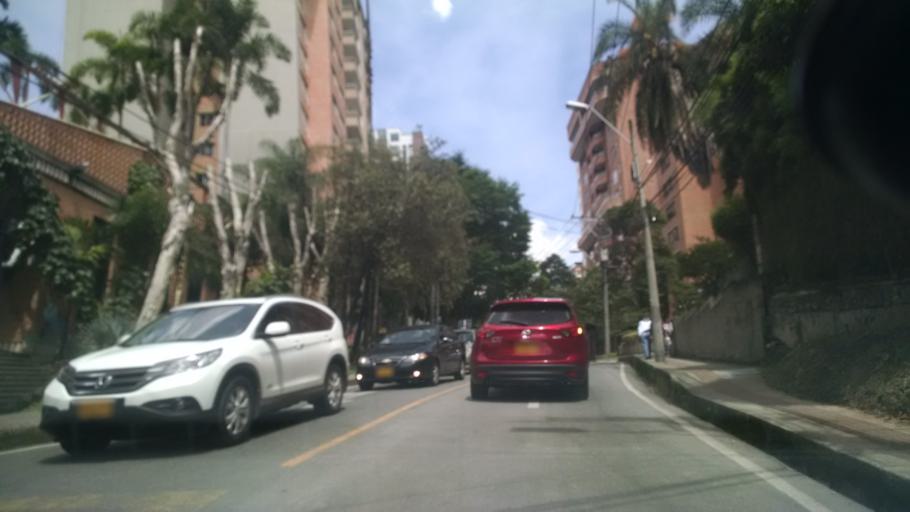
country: CO
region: Antioquia
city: Medellin
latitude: 6.2144
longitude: -75.5688
